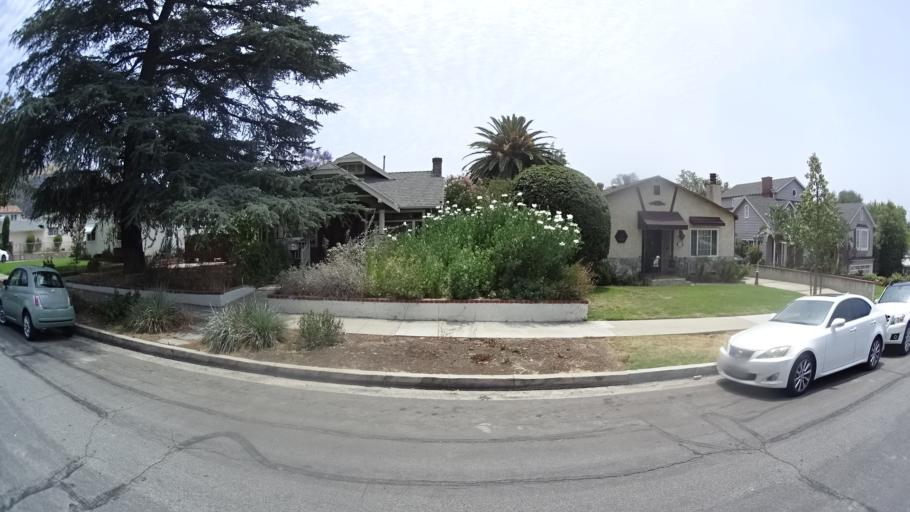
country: US
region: California
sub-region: Los Angeles County
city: Burbank
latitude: 34.1949
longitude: -118.3026
